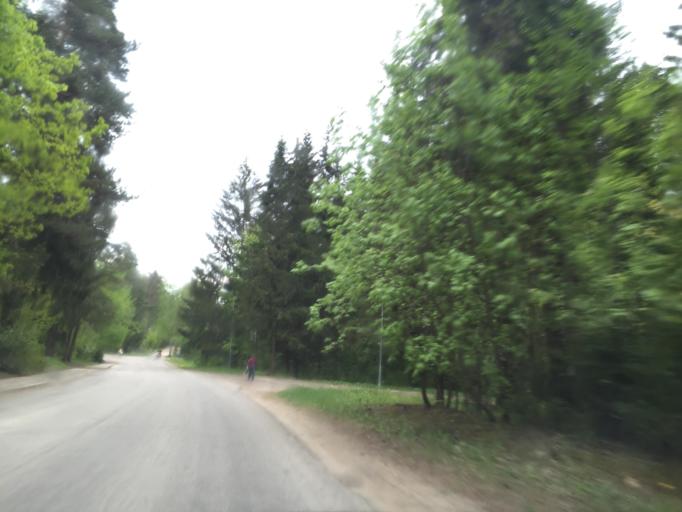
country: LV
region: Ogre
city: Ogre
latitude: 56.8201
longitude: 24.6277
